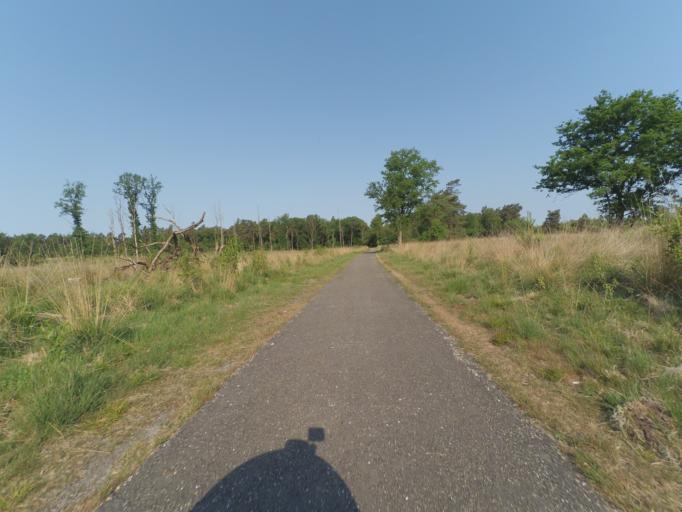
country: NL
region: Gelderland
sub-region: Gemeente Ede
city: Harskamp
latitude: 52.1793
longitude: 5.8305
